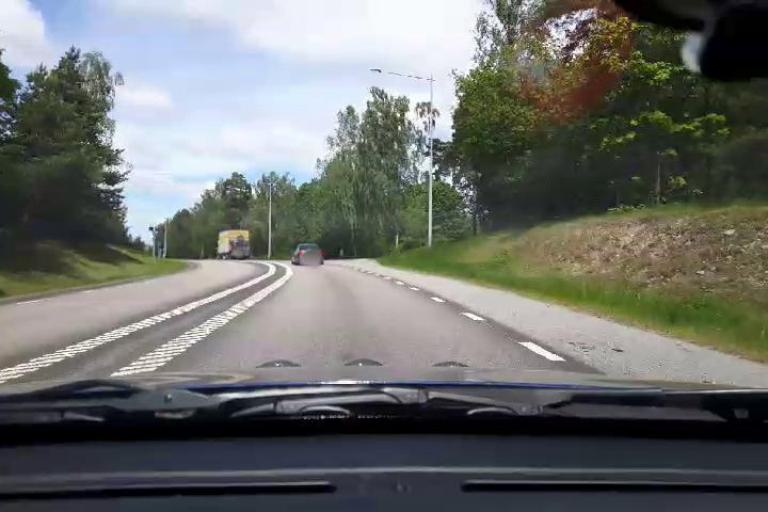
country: SE
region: Uppsala
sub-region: Osthammars Kommun
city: Bjorklinge
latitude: 60.0280
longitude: 17.5536
